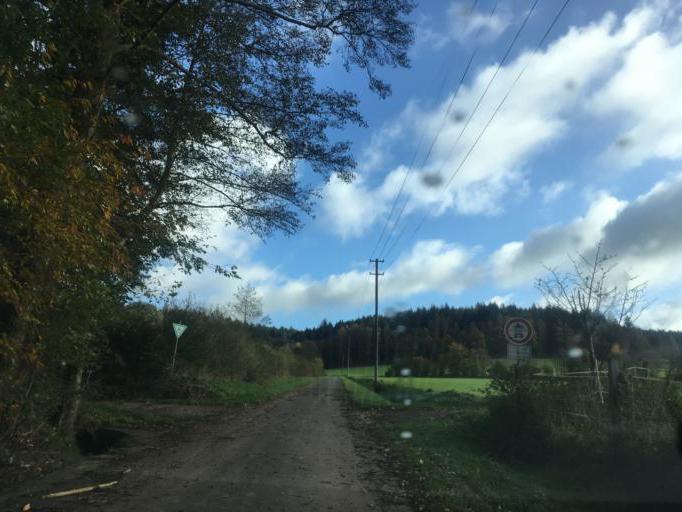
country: DE
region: Lower Saxony
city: Bodenfelde
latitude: 51.6402
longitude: 9.5704
